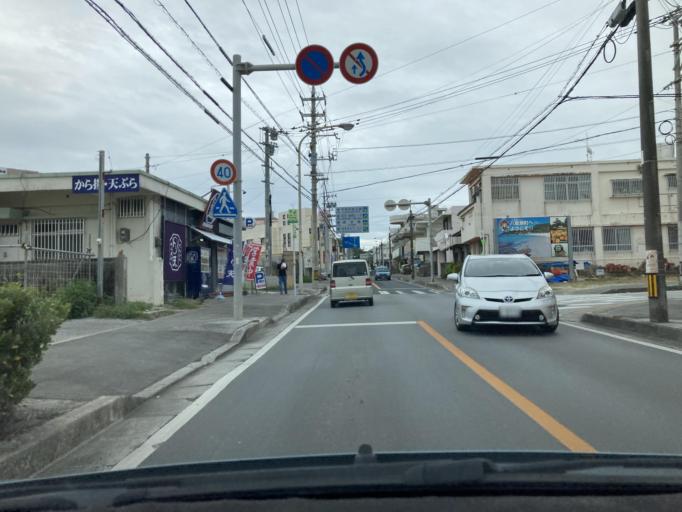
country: JP
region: Okinawa
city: Tomigusuku
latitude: 26.1775
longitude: 127.7185
